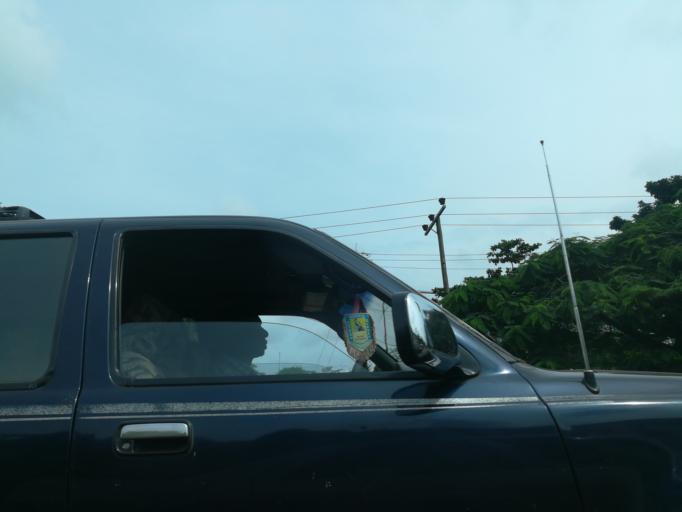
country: NG
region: Lagos
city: Ikeja
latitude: 6.6164
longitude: 3.3585
